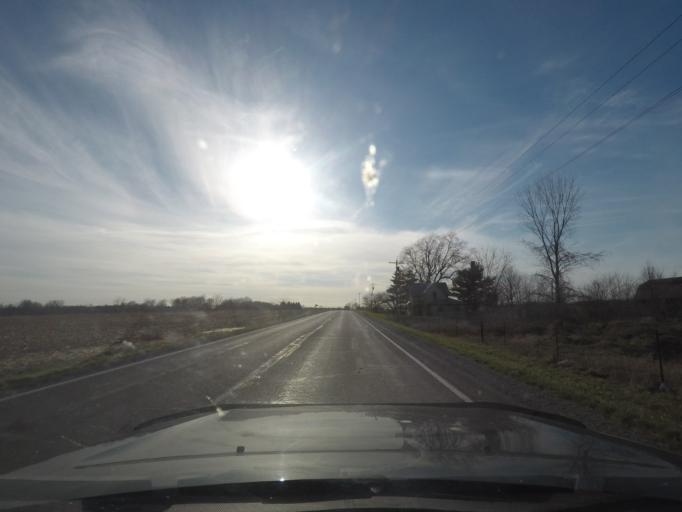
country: US
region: Indiana
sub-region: Marshall County
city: Plymouth
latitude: 41.4489
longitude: -86.3425
